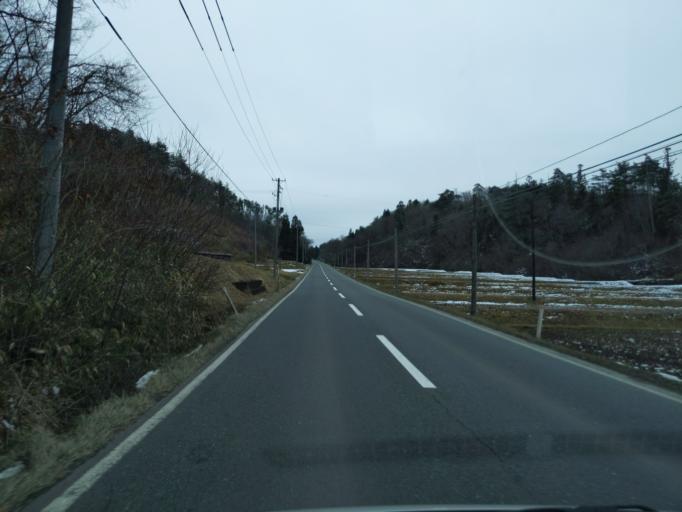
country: JP
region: Iwate
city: Mizusawa
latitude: 39.1491
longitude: 141.2429
